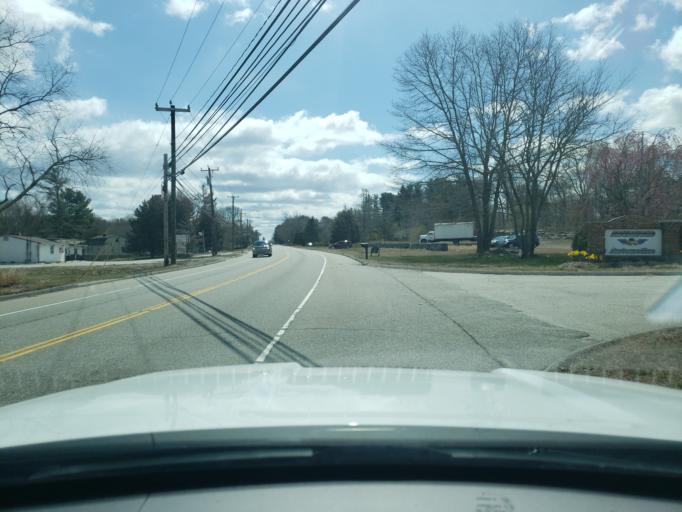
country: US
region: Connecticut
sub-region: New London County
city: Jewett City
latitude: 41.5890
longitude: -71.9533
